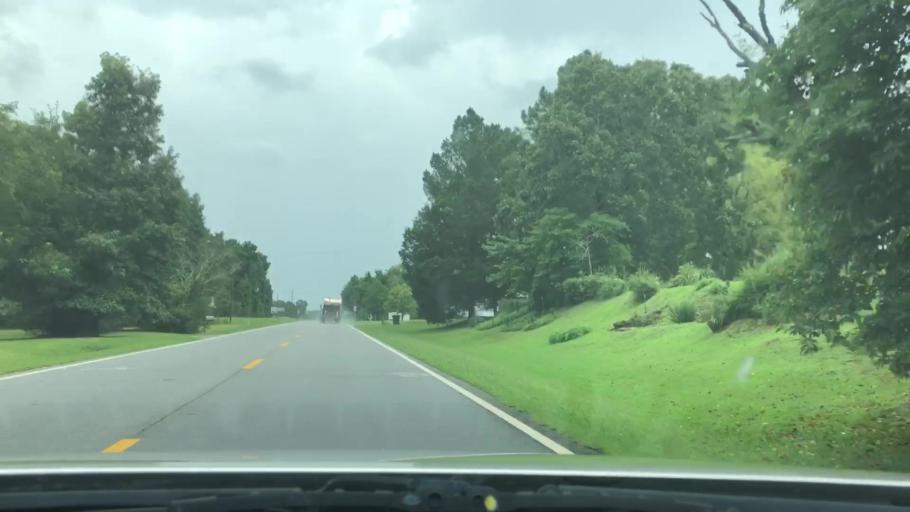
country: US
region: Georgia
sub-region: Lamar County
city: Barnesville
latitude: 33.0733
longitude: -84.2433
